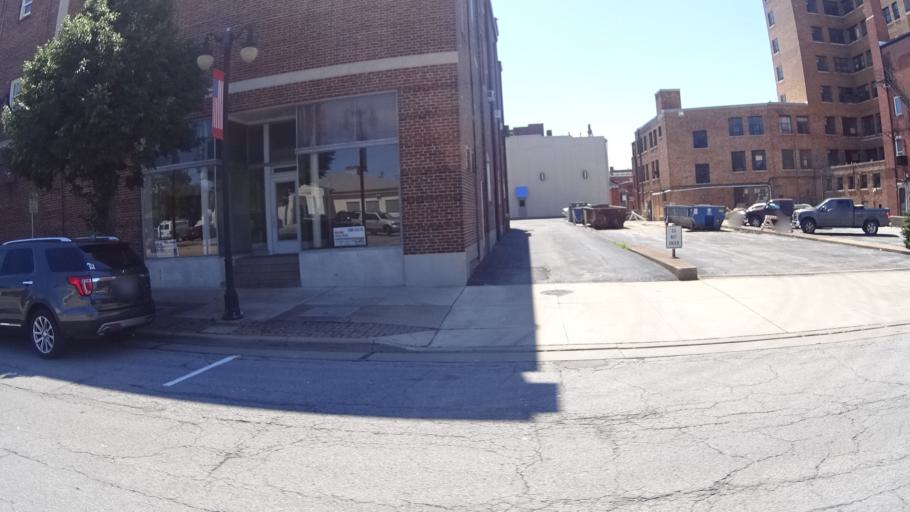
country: US
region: Ohio
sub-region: Erie County
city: Sandusky
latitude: 41.4561
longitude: -82.7097
